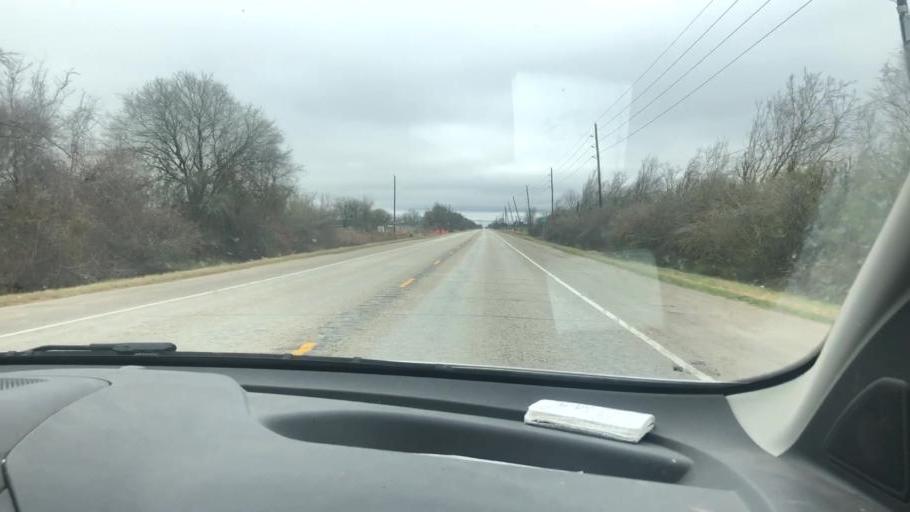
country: US
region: Texas
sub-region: Wharton County
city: Wharton
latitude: 29.2816
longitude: -96.0668
